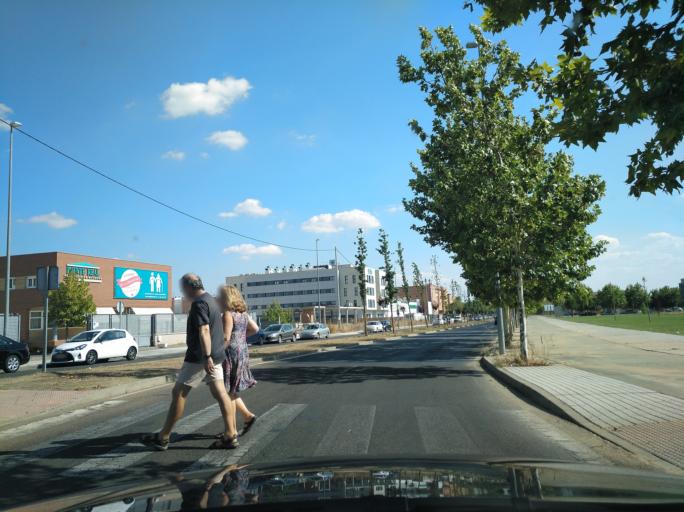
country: ES
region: Extremadura
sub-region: Provincia de Badajoz
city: Badajoz
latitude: 38.8908
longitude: -6.9990
